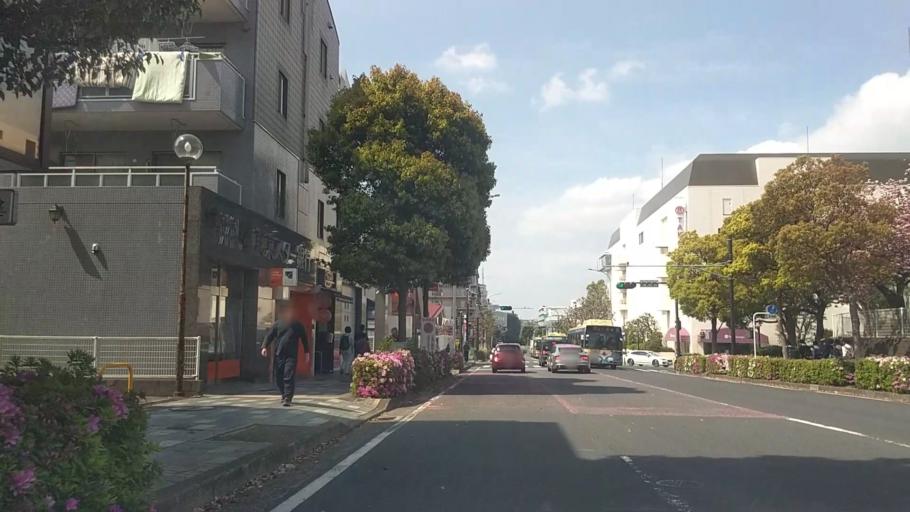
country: JP
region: Kanagawa
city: Kamakura
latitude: 35.3731
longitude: 139.5772
